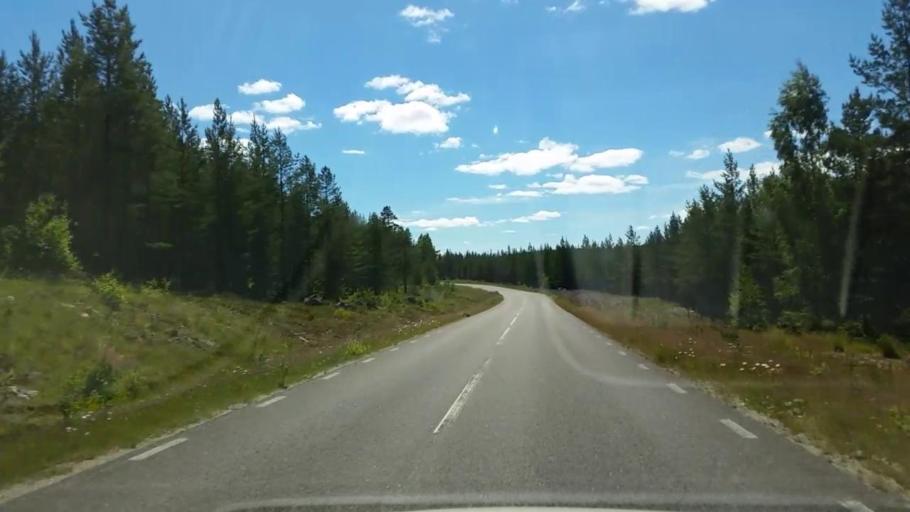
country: SE
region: Gaevleborg
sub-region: Ljusdals Kommun
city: Farila
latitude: 61.6181
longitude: 15.5447
